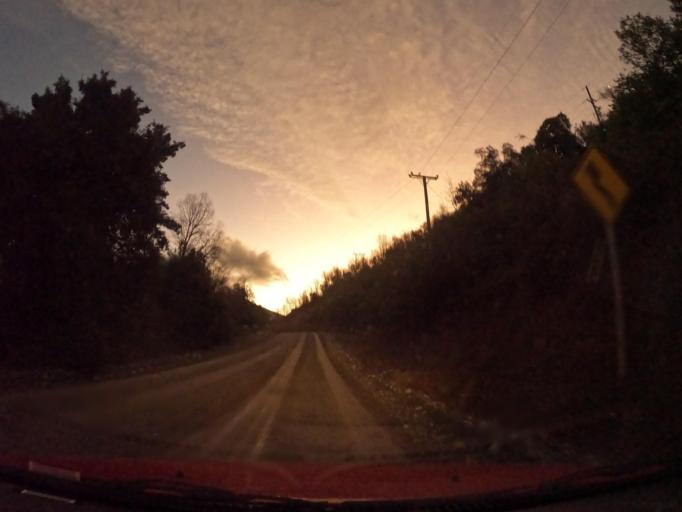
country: CL
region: Maule
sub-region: Provincia de Linares
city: Colbun
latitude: -35.8584
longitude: -71.2381
